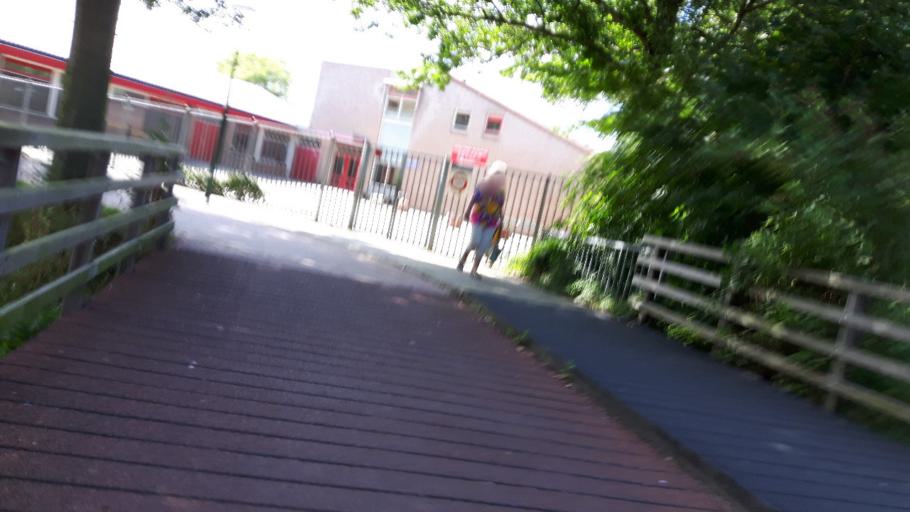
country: NL
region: Utrecht
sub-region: Stichtse Vecht
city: Spechtenkamp
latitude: 52.1415
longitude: 5.0116
